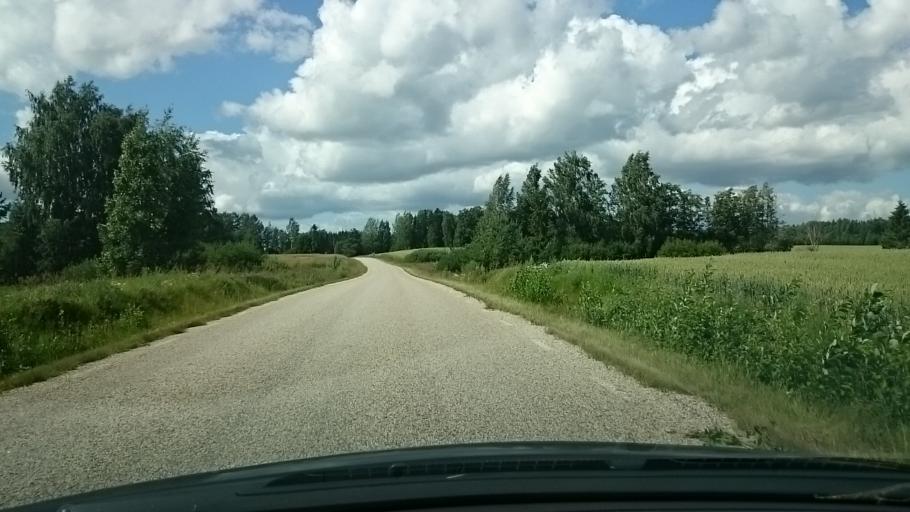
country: EE
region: Vorumaa
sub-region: Voru linn
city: Voru
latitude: 57.9169
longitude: 27.1697
